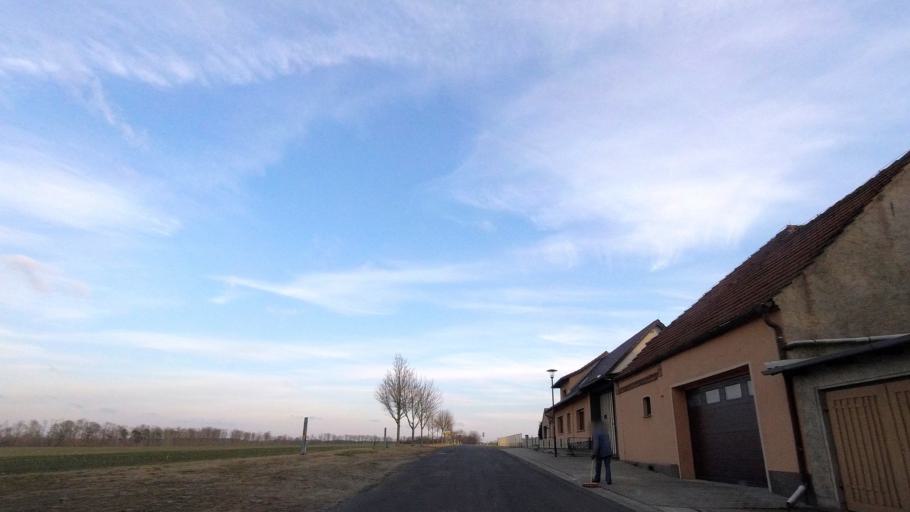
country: DE
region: Brandenburg
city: Niemegk
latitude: 52.0795
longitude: 12.6470
